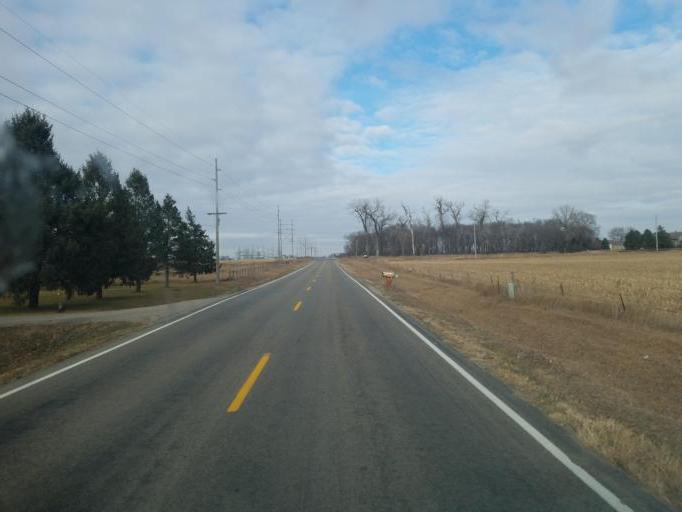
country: US
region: Nebraska
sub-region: Madison County
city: Norfolk
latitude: 42.0602
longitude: -97.4070
